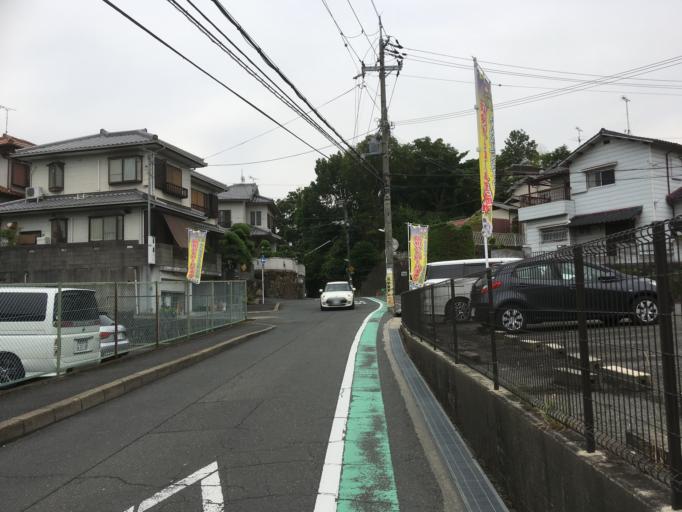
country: JP
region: Nara
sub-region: Ikoma-shi
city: Ikoma
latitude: 34.6985
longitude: 135.7035
